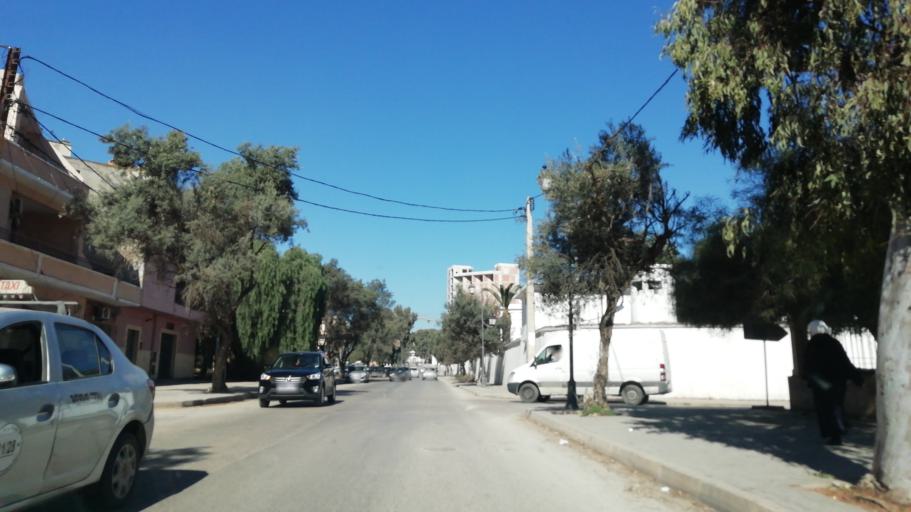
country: DZ
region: Oran
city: Oran
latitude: 35.6937
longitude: -0.6107
